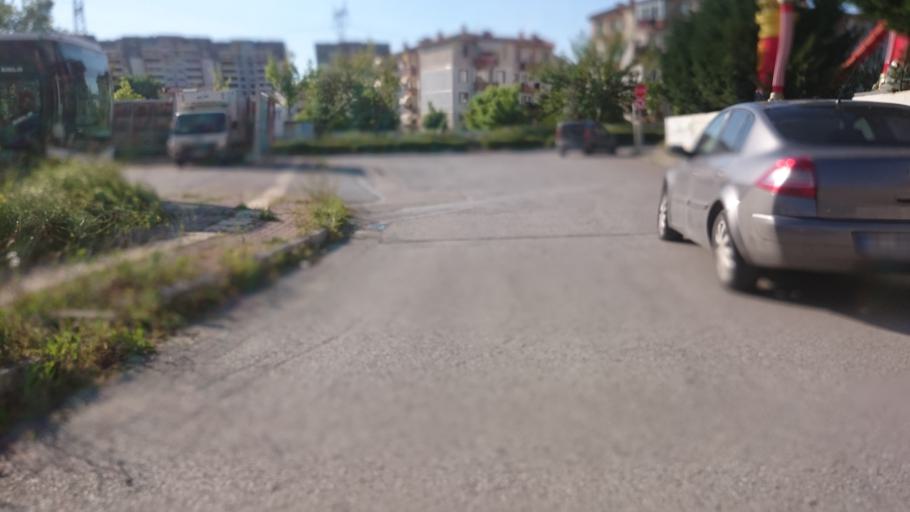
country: TR
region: Bursa
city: Niluefer
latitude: 40.2245
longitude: 28.9651
